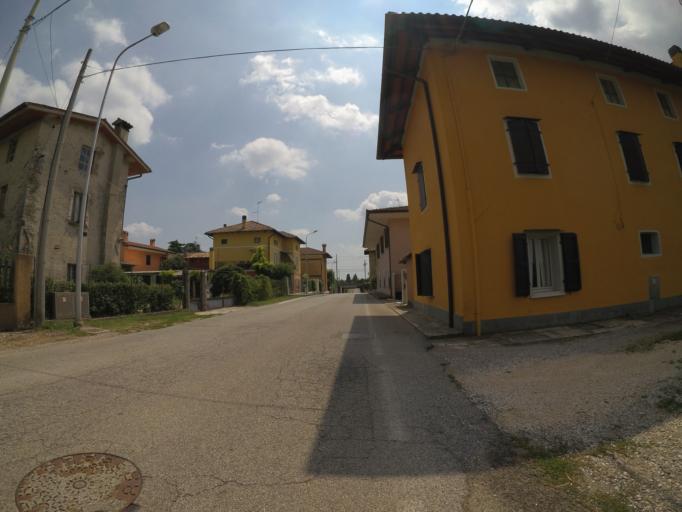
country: IT
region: Friuli Venezia Giulia
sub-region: Provincia di Udine
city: Basiliano
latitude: 46.0020
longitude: 13.0753
